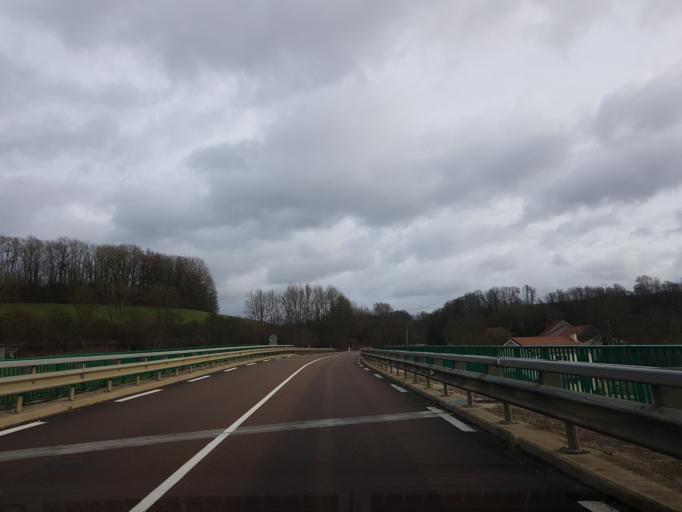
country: FR
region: Champagne-Ardenne
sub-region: Departement de la Haute-Marne
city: Langres
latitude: 47.8575
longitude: 5.3715
